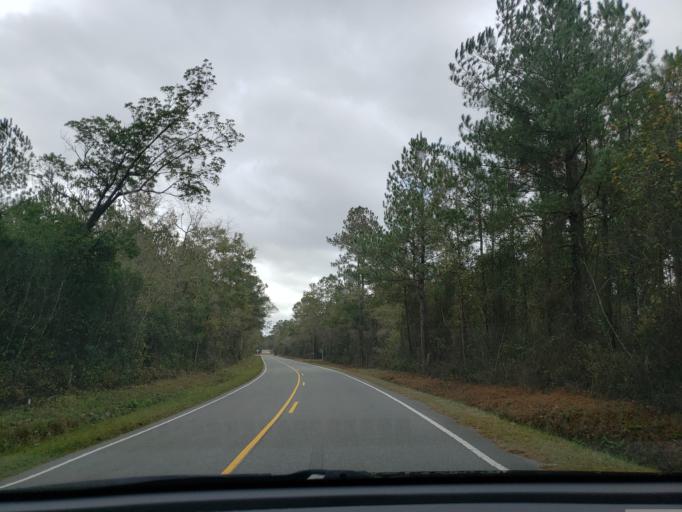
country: US
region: North Carolina
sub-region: Onslow County
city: Richlands
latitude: 34.7215
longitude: -77.6226
